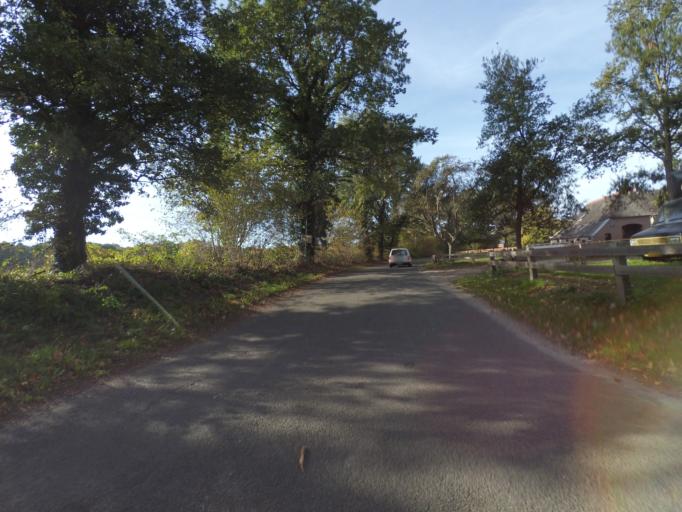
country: NL
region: Gelderland
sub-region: Gemeente Lochem
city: Epse
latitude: 52.2339
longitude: 6.2430
